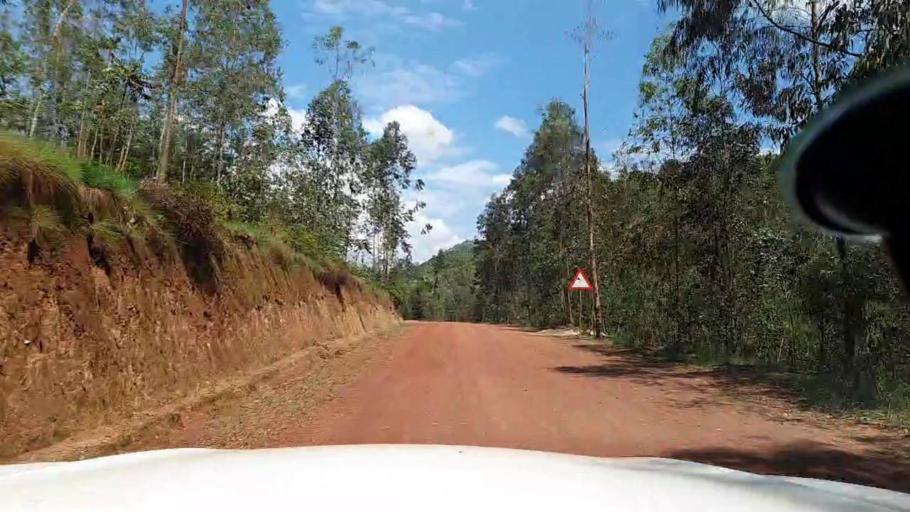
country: RW
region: Kigali
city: Kigali
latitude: -1.7622
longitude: 29.8721
